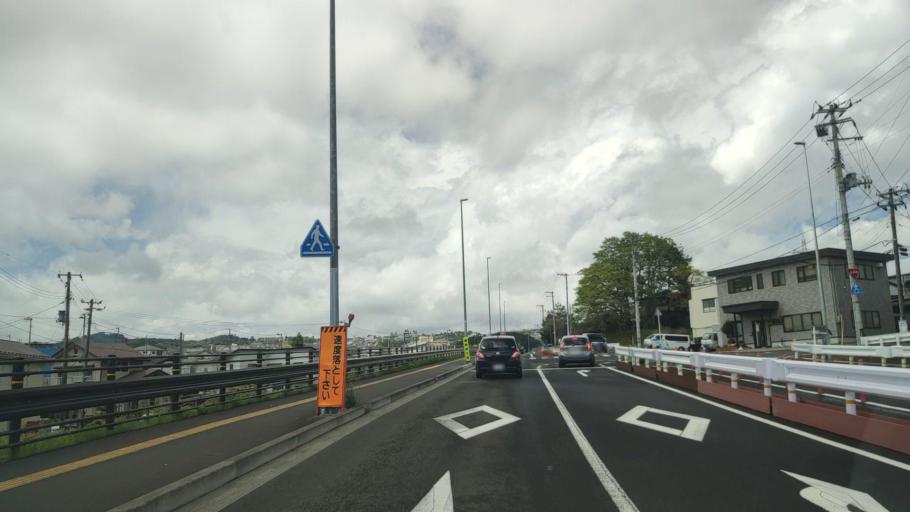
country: JP
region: Miyagi
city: Sendai
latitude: 38.2274
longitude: 140.8586
